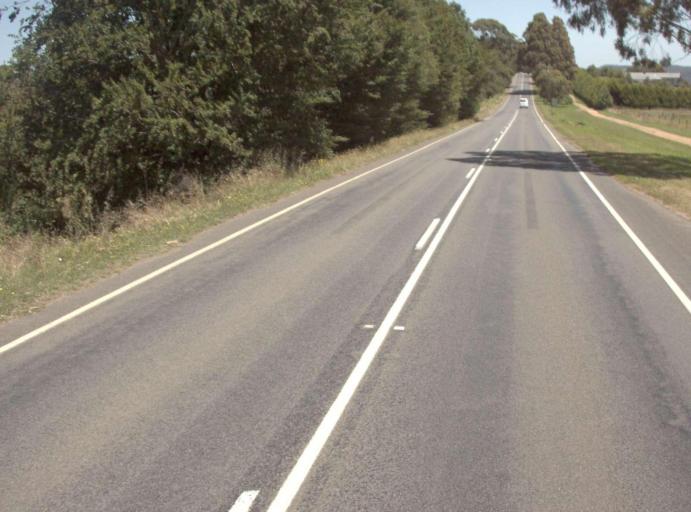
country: AU
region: Victoria
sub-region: Baw Baw
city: Warragul
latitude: -37.9707
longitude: 145.9528
